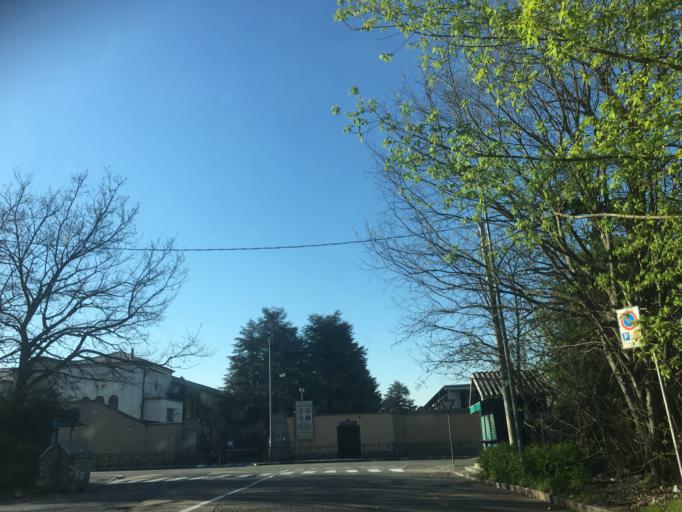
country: IT
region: Piedmont
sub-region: Provincia di Torino
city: Turin
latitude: 45.0780
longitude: 7.7106
